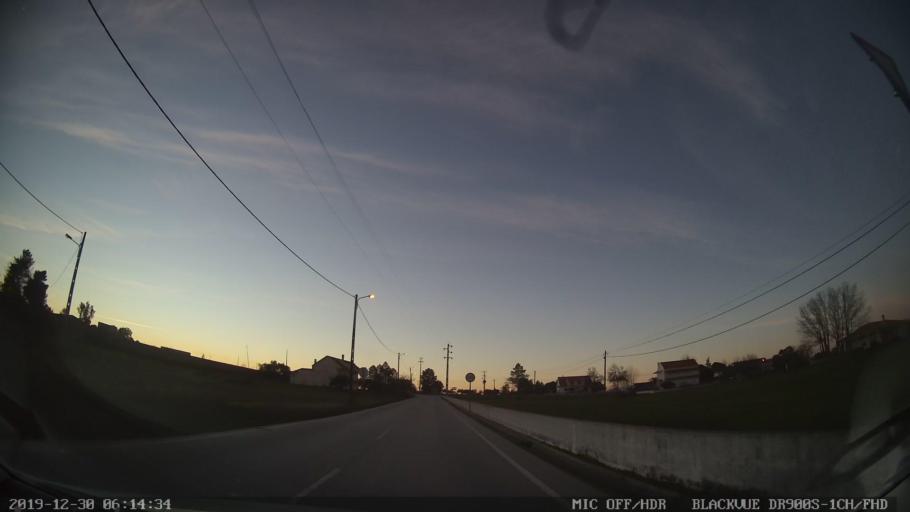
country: PT
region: Castelo Branco
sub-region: Penamacor
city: Penamacor
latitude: 40.1129
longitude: -7.2188
